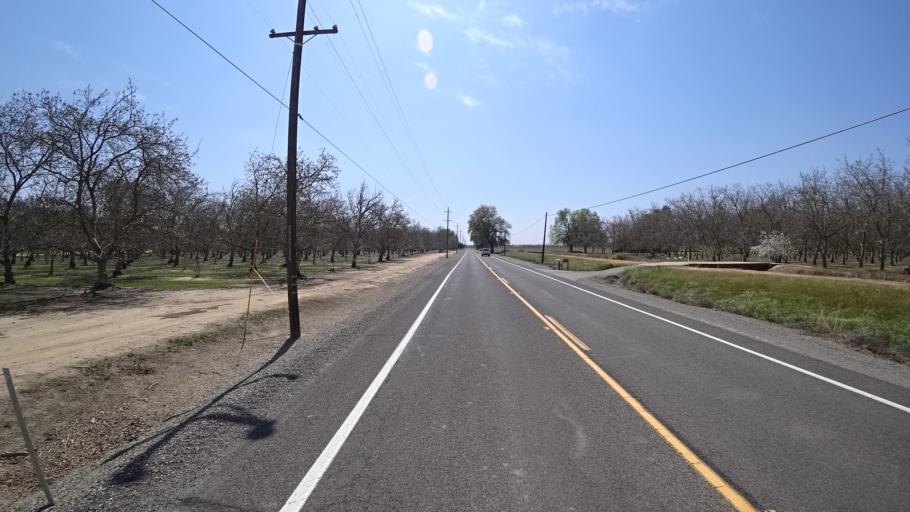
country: US
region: California
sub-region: Glenn County
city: Willows
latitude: 39.4760
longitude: -122.0188
